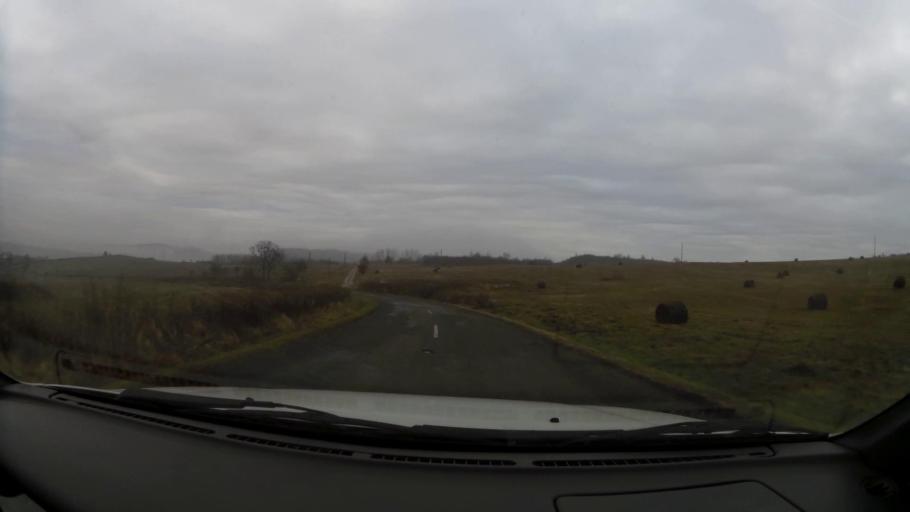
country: HU
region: Borsod-Abauj-Zemplen
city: Rudabanya
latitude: 48.3966
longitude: 20.6261
